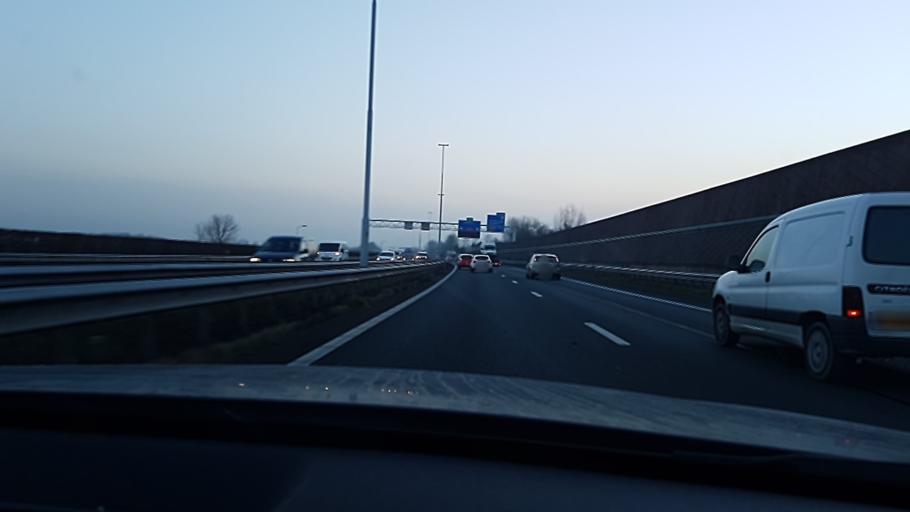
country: NL
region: North Brabant
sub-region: Gemeente Woudrichem
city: Almkerk
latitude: 51.7806
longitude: 4.9275
